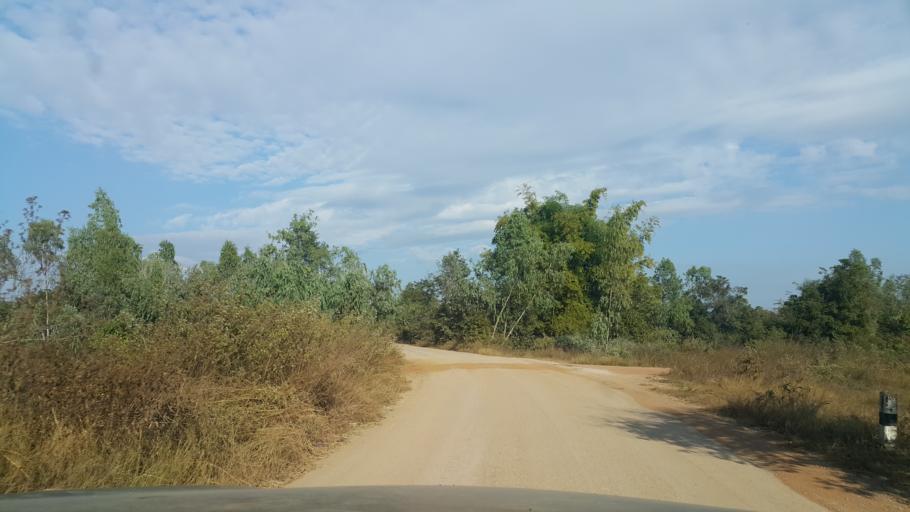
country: TH
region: Lampang
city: Hang Chat
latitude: 18.2743
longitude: 99.3578
